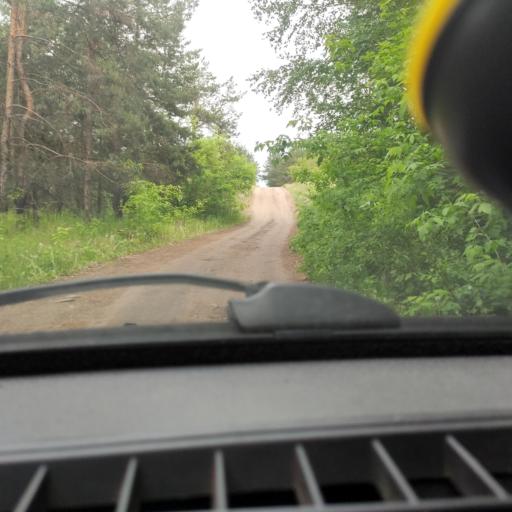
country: RU
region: Samara
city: Zhigulevsk
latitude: 53.5032
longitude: 49.5066
